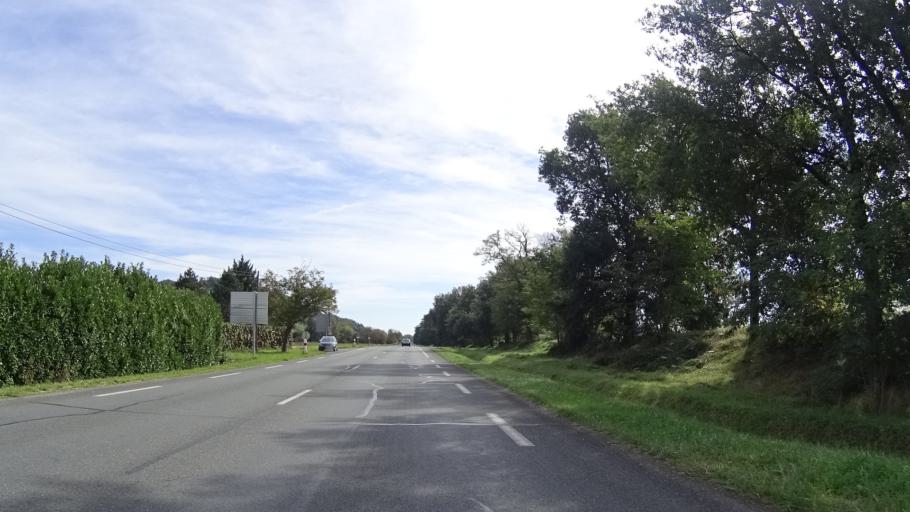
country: FR
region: Midi-Pyrenees
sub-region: Departement du Tarn-et-Garonne
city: Lamagistere
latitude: 44.1481
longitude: 0.7618
